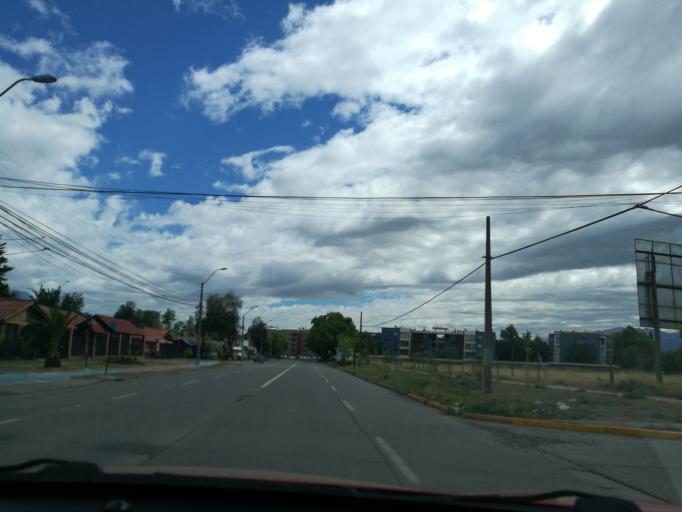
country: CL
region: O'Higgins
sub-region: Provincia de Cachapoal
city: Rancagua
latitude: -34.1421
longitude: -70.7351
